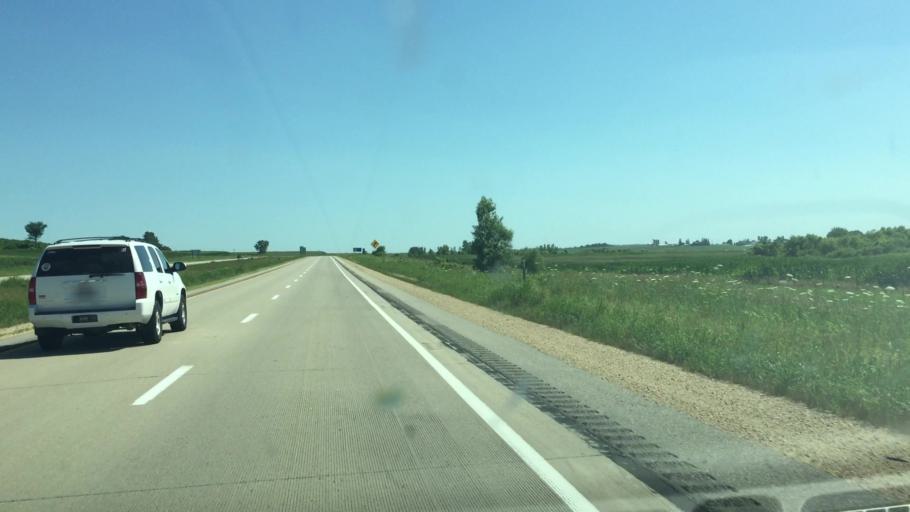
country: US
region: Iowa
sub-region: Jones County
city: Monticello
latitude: 42.2167
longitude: -91.1735
